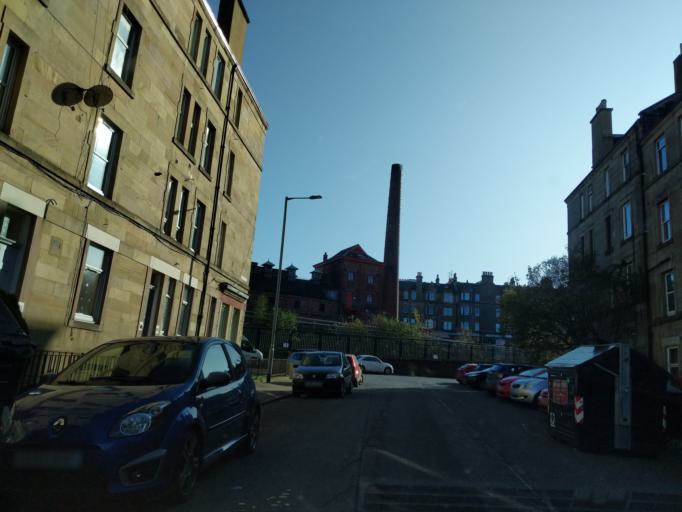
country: GB
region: Scotland
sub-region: Edinburgh
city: Colinton
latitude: 55.9361
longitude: -3.2324
